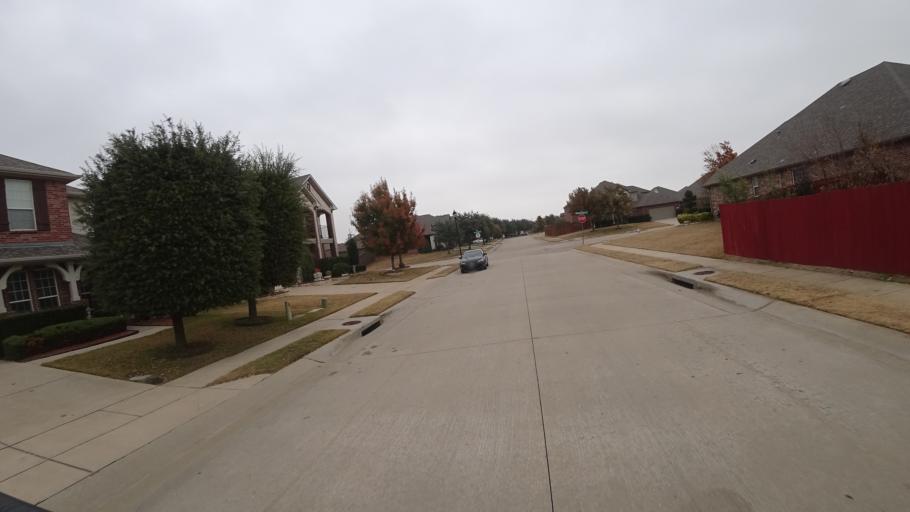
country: US
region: Texas
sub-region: Denton County
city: The Colony
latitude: 33.0672
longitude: -96.9056
